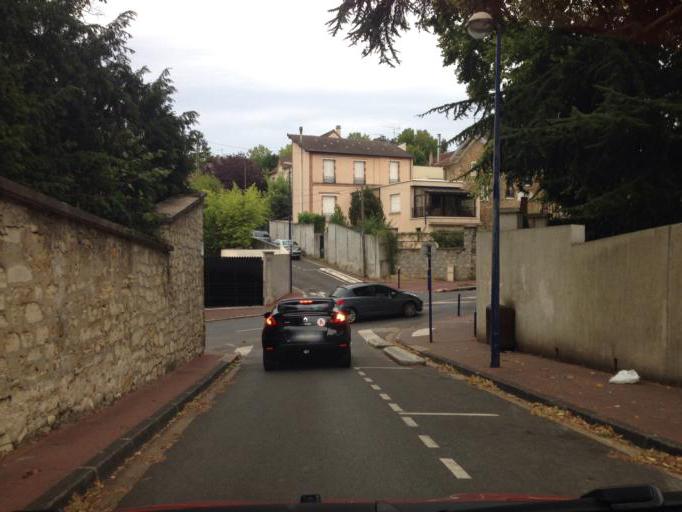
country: FR
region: Ile-de-France
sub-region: Departement des Hauts-de-Seine
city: Clamart
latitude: 48.7965
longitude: 2.2647
